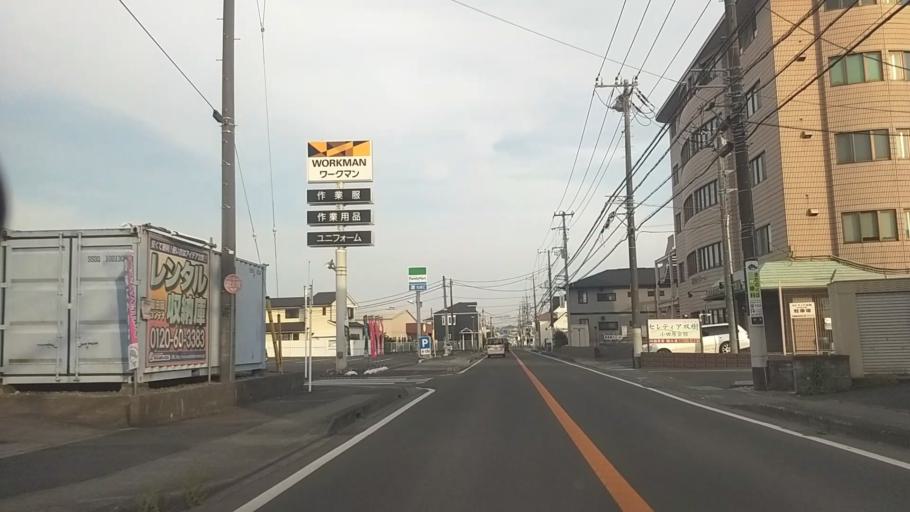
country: JP
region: Kanagawa
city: Odawara
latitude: 35.2896
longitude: 139.1364
